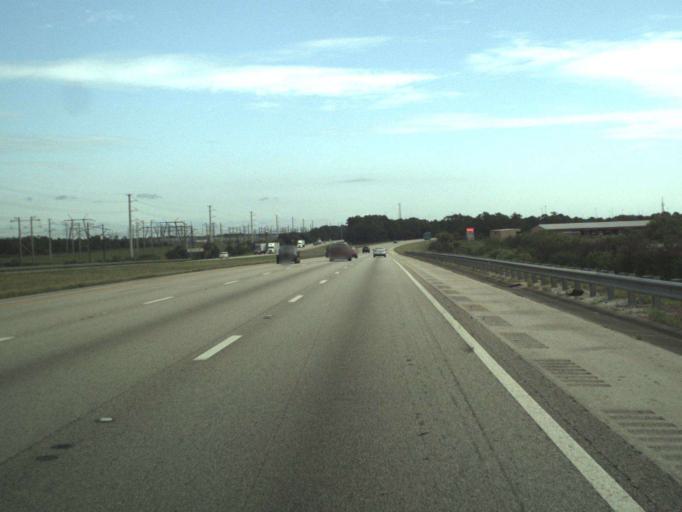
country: US
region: Florida
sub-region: Saint Lucie County
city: River Park
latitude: 27.3566
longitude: -80.4139
